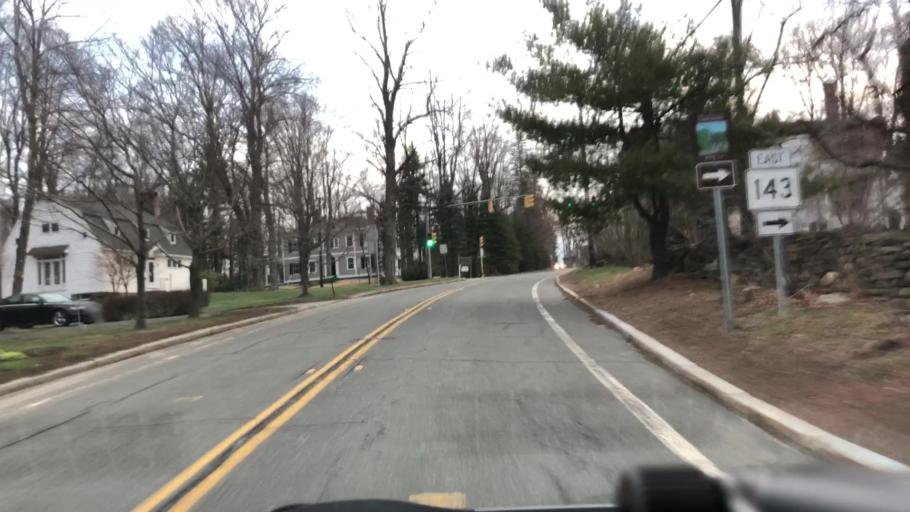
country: US
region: Massachusetts
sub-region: Hampshire County
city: Chesterfield
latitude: 42.4097
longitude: -72.9373
